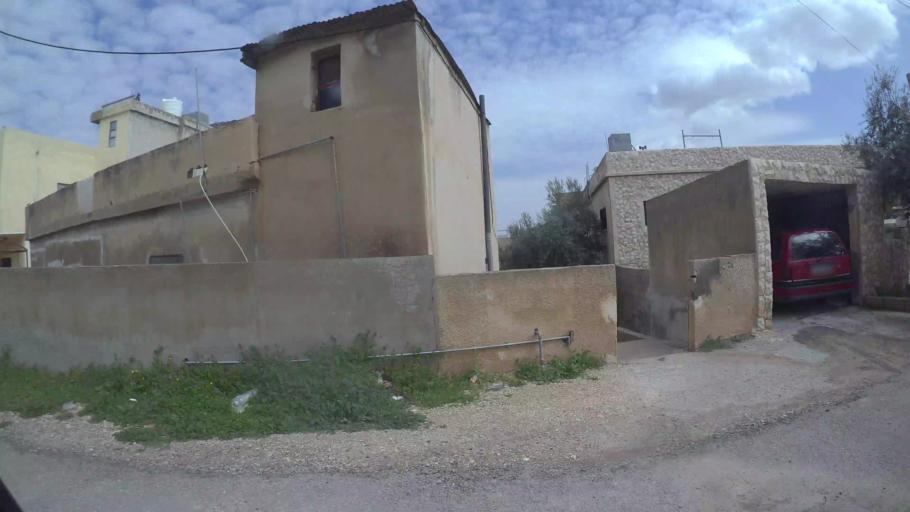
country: JO
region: Amman
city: Al Jubayhah
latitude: 32.0657
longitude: 35.8334
